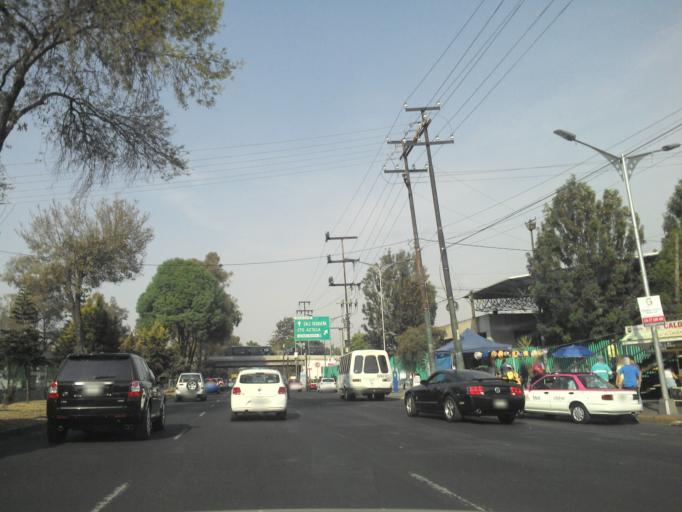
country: MX
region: Mexico City
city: Tlalpan
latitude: 19.3012
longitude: -99.1472
